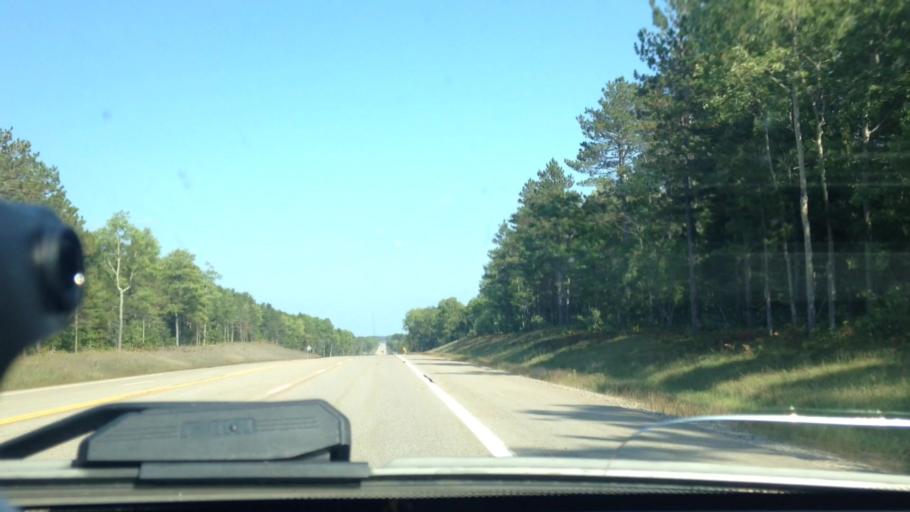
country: US
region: Michigan
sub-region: Chippewa County
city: Sault Ste. Marie
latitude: 46.3632
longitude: -84.7704
